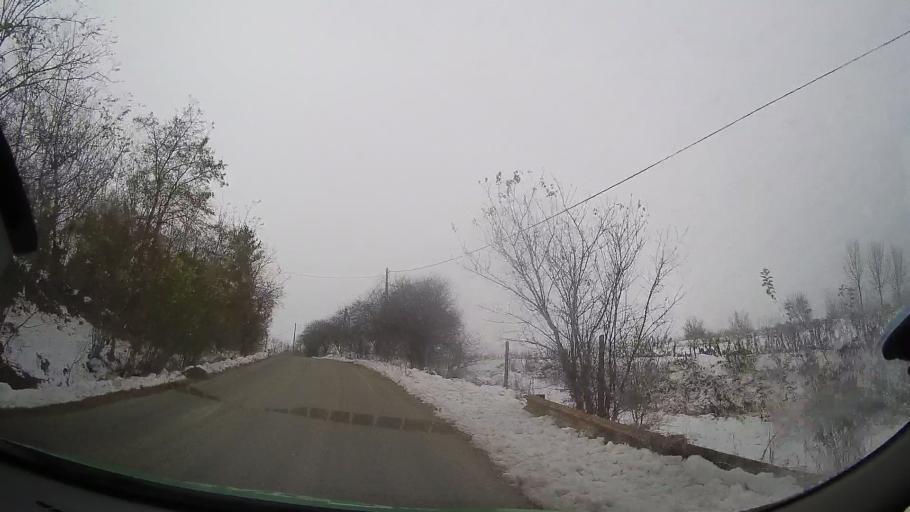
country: RO
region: Bacau
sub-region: Comuna Glavanesti
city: Frumuselu
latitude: 46.2700
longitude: 27.3051
